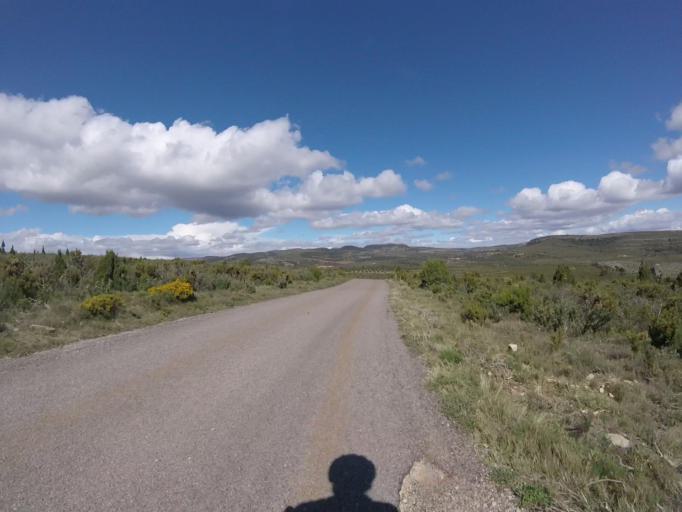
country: ES
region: Valencia
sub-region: Provincia de Castello
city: Culla
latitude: 40.3056
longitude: -0.1163
